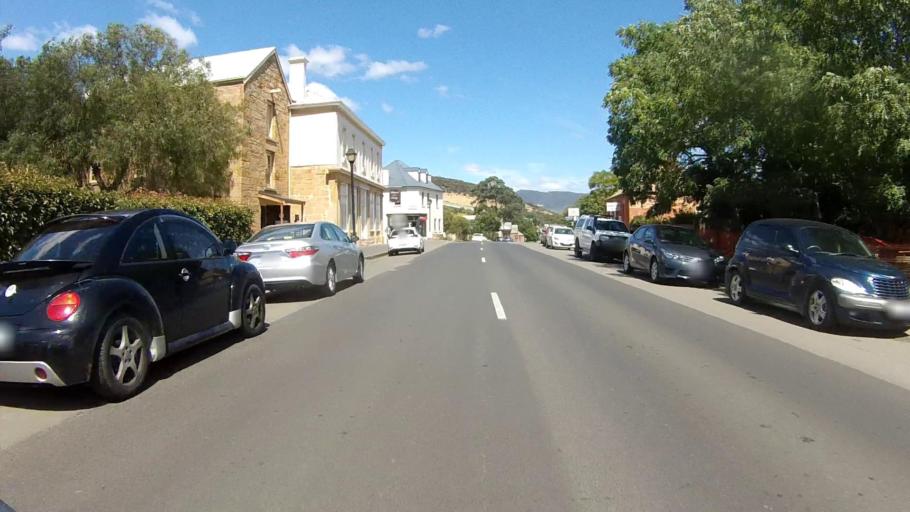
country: AU
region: Tasmania
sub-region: Clarence
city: Cambridge
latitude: -42.7363
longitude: 147.4362
